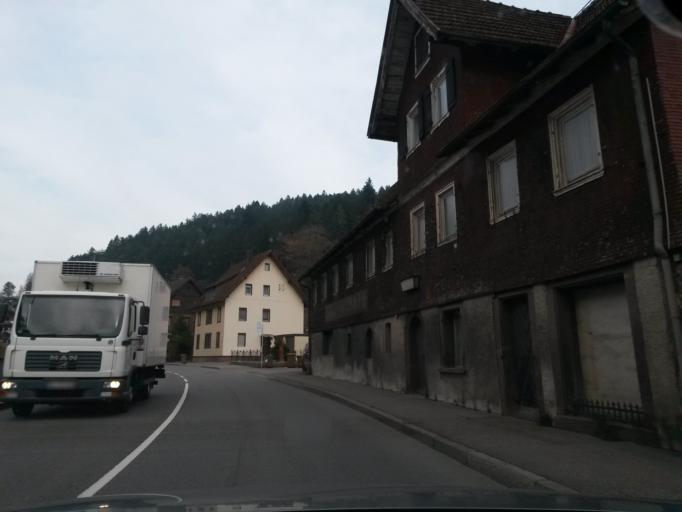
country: DE
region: Baden-Wuerttemberg
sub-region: Karlsruhe Region
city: Alpirsbach
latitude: 48.3310
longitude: 8.3971
